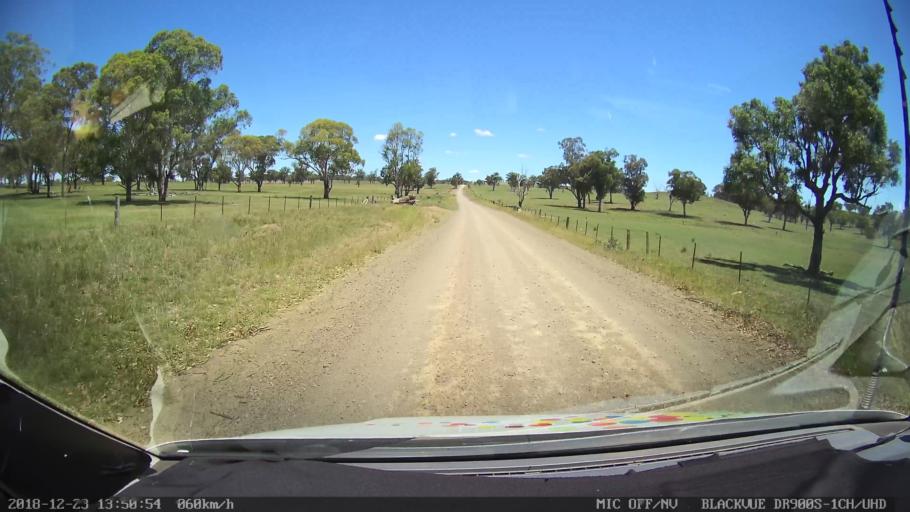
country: AU
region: New South Wales
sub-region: Tamworth Municipality
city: Manilla
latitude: -30.5347
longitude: 151.1059
